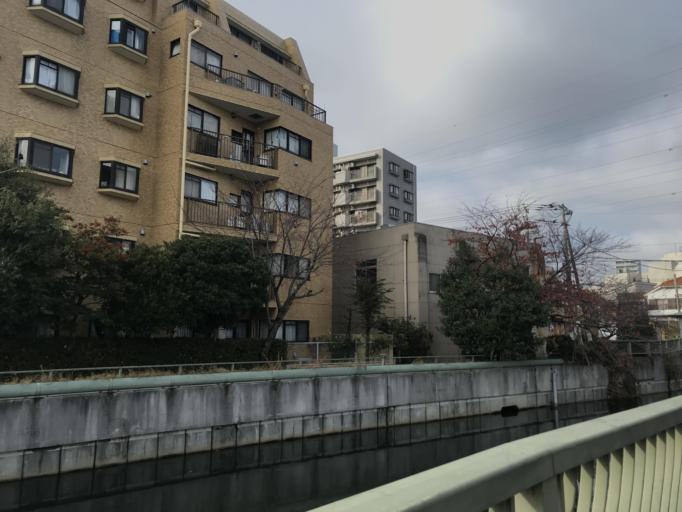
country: JP
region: Chiba
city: Funabashi
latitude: 35.7033
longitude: 139.9909
